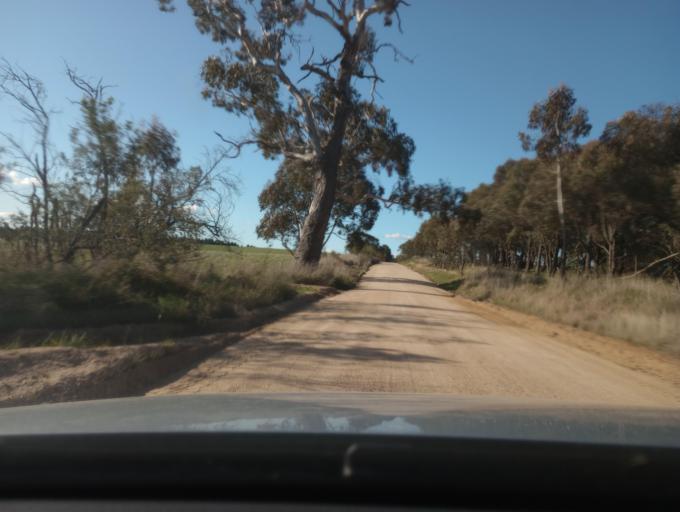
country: AU
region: New South Wales
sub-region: Blayney
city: Millthorpe
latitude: -33.3978
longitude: 149.3090
